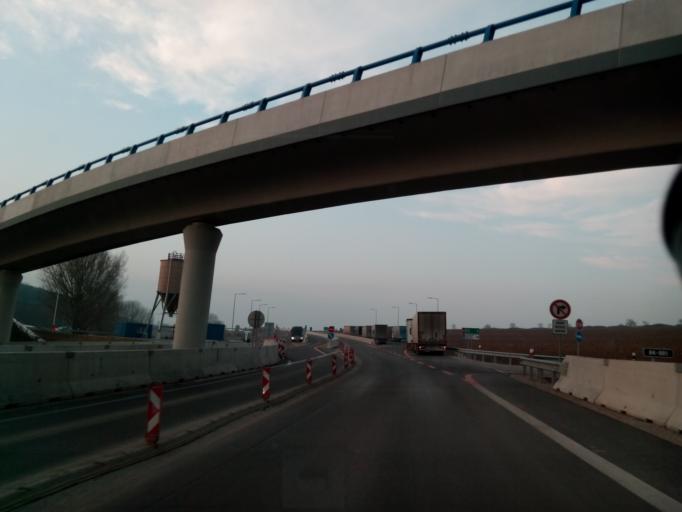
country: HU
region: Borsod-Abauj-Zemplen
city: Gonc
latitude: 48.5324
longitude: 21.2523
